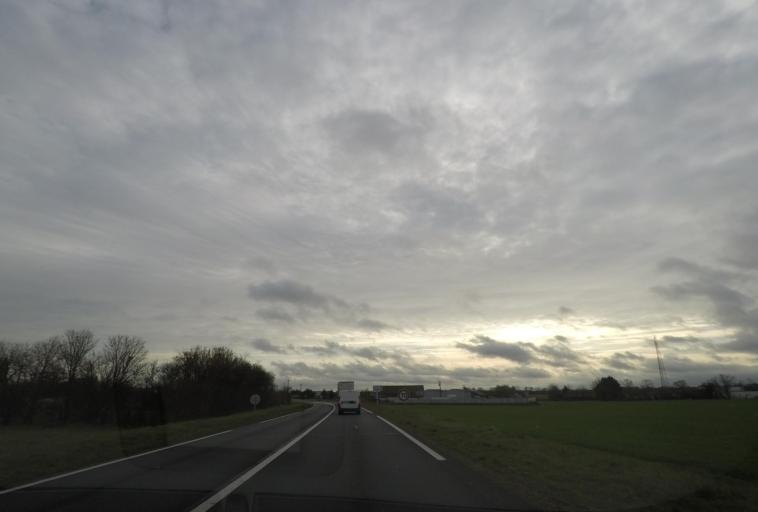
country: FR
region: Centre
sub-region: Departement du Loir-et-Cher
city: Sarge-sur-Braye
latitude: 47.8998
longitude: 0.9241
